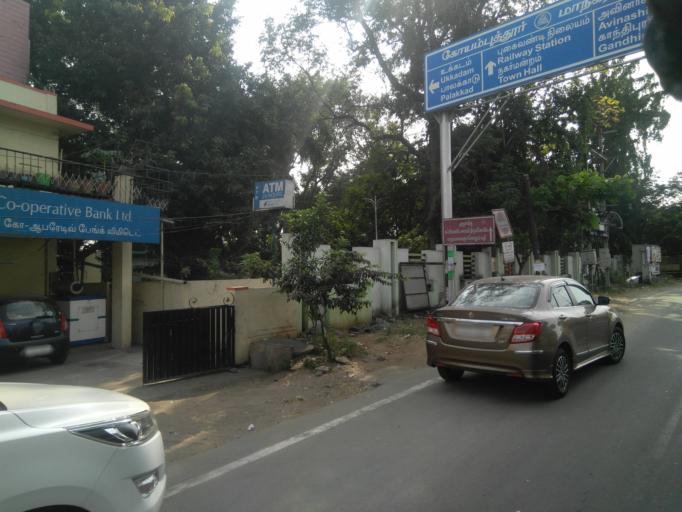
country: IN
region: Tamil Nadu
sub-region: Coimbatore
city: Coimbatore
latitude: 10.9977
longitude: 76.9860
